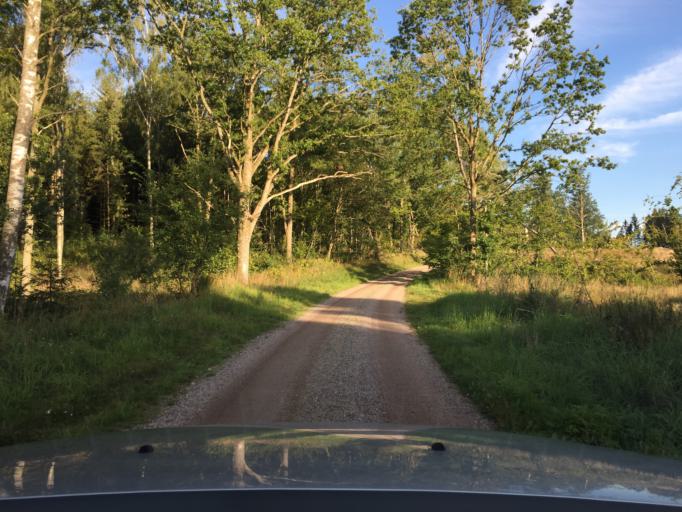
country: SE
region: Skane
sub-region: Hassleholms Kommun
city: Sosdala
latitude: 56.0213
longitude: 13.7069
